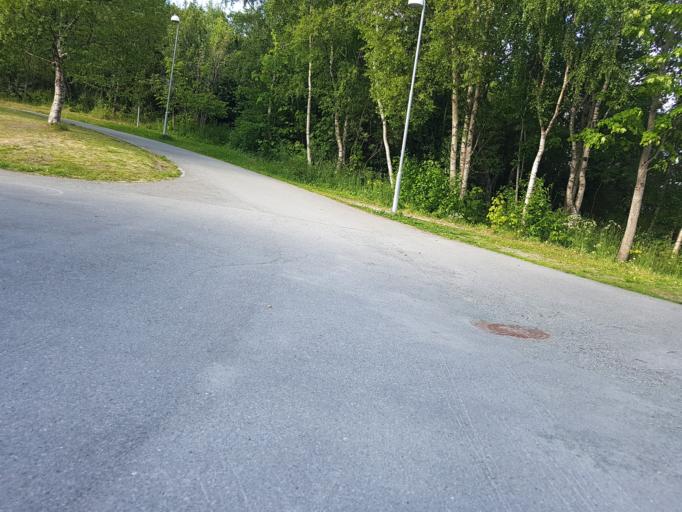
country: NO
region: Sor-Trondelag
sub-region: Trondheim
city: Trondheim
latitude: 63.4184
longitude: 10.3671
